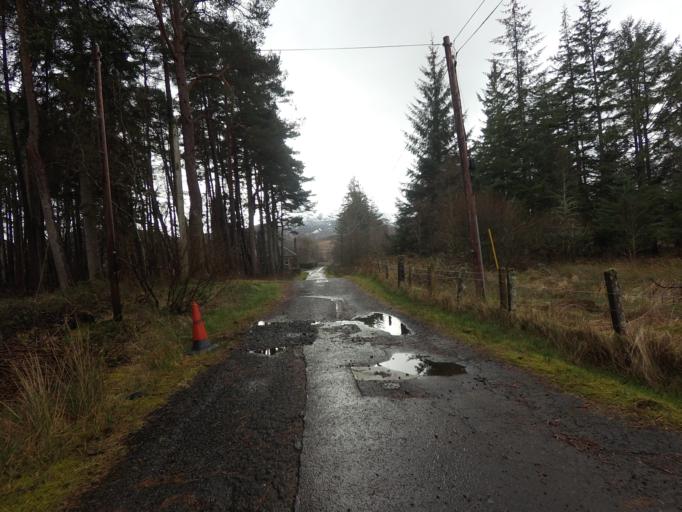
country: GB
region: Scotland
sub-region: West Dunbartonshire
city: Balloch
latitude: 56.2577
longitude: -4.5823
